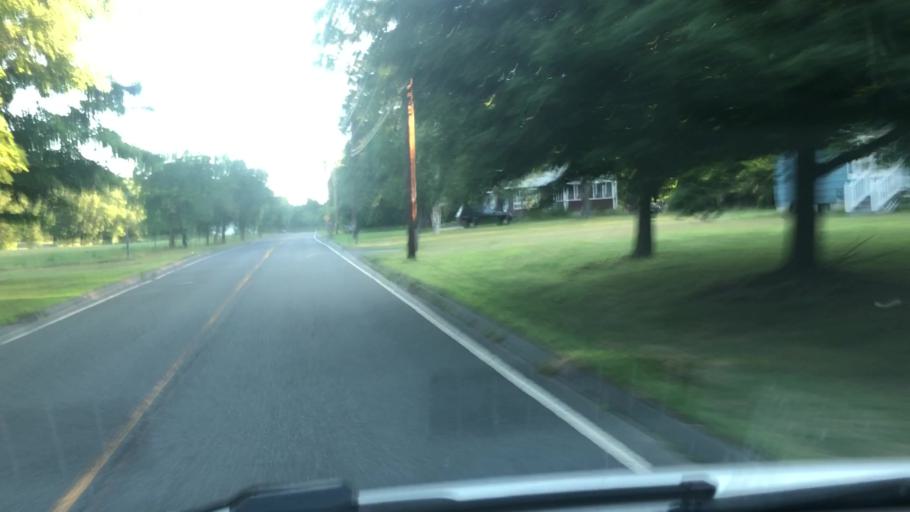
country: US
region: Massachusetts
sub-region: Hampshire County
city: Westhampton
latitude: 42.3008
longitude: -72.7167
